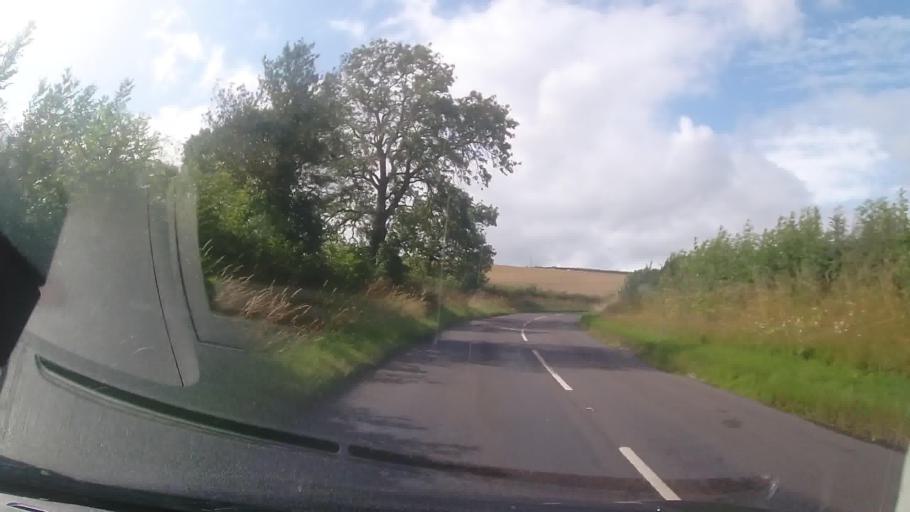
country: GB
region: Wales
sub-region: Sir Powys
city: Knighton
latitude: 52.3889
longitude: -3.0404
